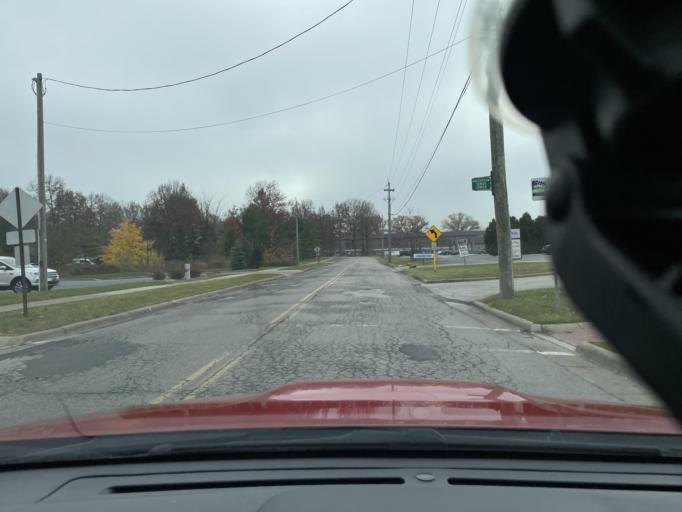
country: US
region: Ohio
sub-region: Mahoning County
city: Austintown
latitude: 41.0974
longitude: -80.7486
